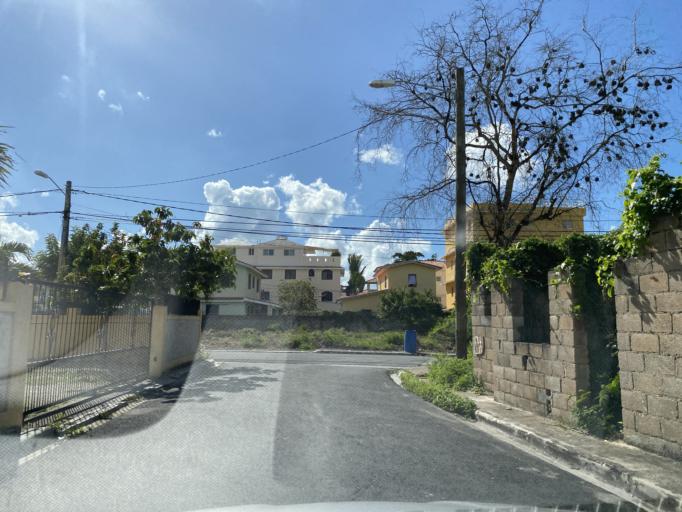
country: DO
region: La Romana
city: La Romana
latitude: 18.3686
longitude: -68.8371
